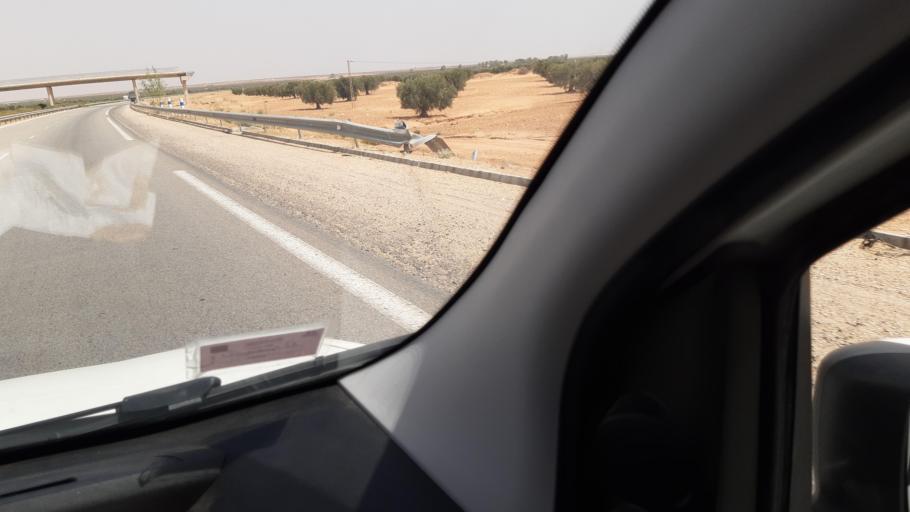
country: TN
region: Safaqis
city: Bi'r `Ali Bin Khalifah
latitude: 34.5308
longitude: 10.0935
